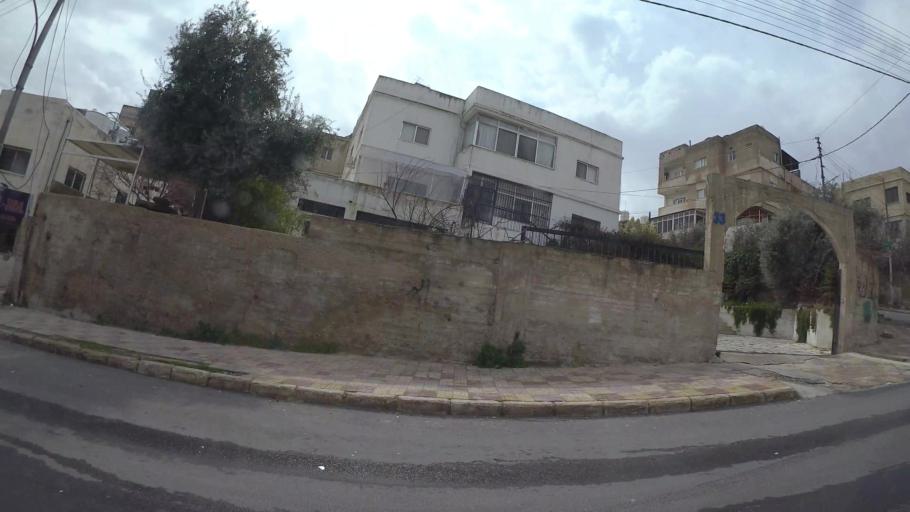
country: JO
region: Amman
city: Amman
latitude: 31.9617
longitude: 35.9544
